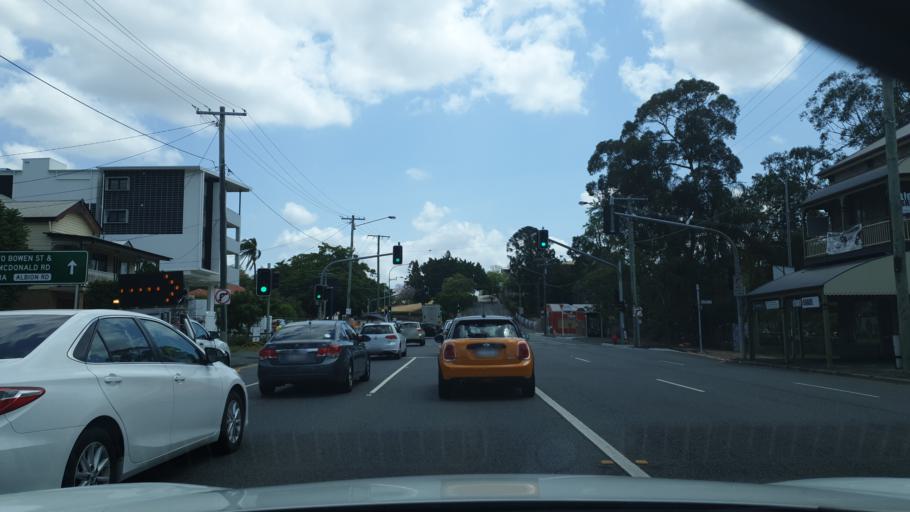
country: AU
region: Queensland
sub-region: Brisbane
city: Windsor
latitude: -27.4337
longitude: 153.0318
